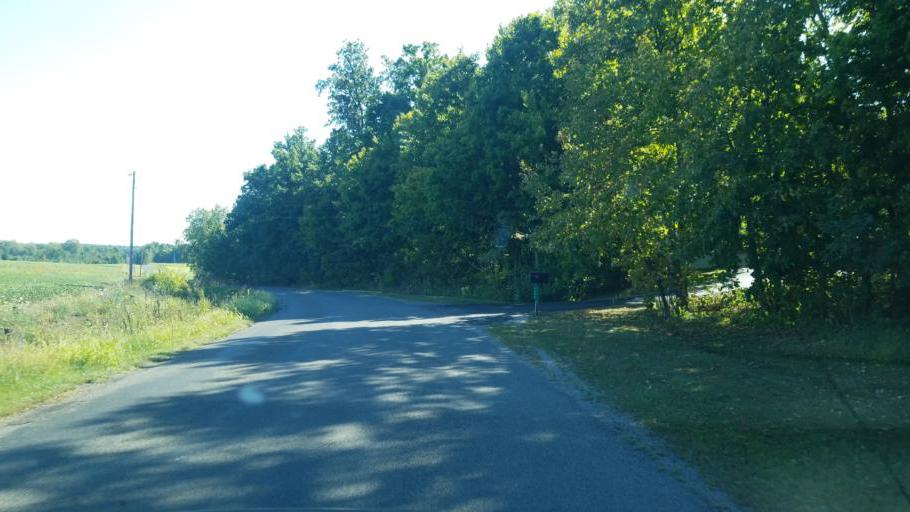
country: US
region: Ohio
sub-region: Champaign County
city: North Lewisburg
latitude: 40.1853
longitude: -83.6169
